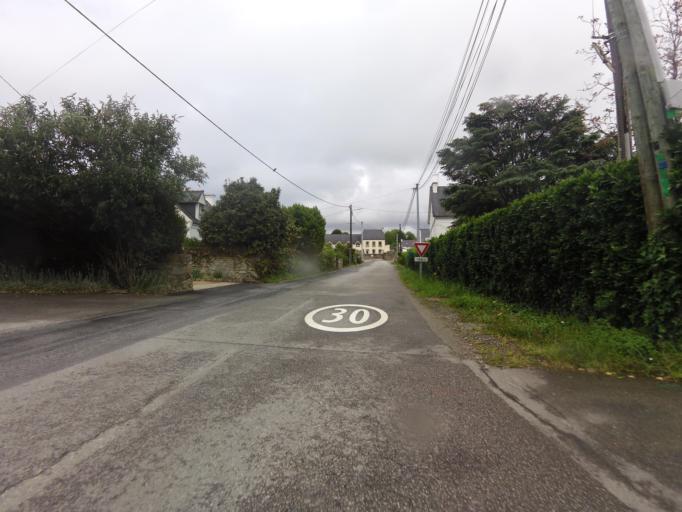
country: FR
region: Brittany
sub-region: Departement du Morbihan
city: Baden
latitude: 47.6178
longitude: -2.9229
